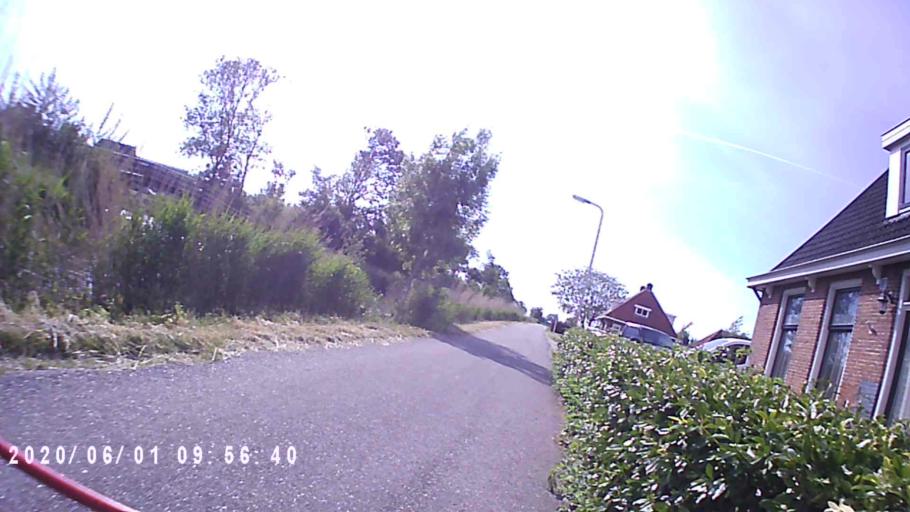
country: NL
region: Friesland
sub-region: Menameradiel
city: Berltsum
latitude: 53.2373
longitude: 5.6478
